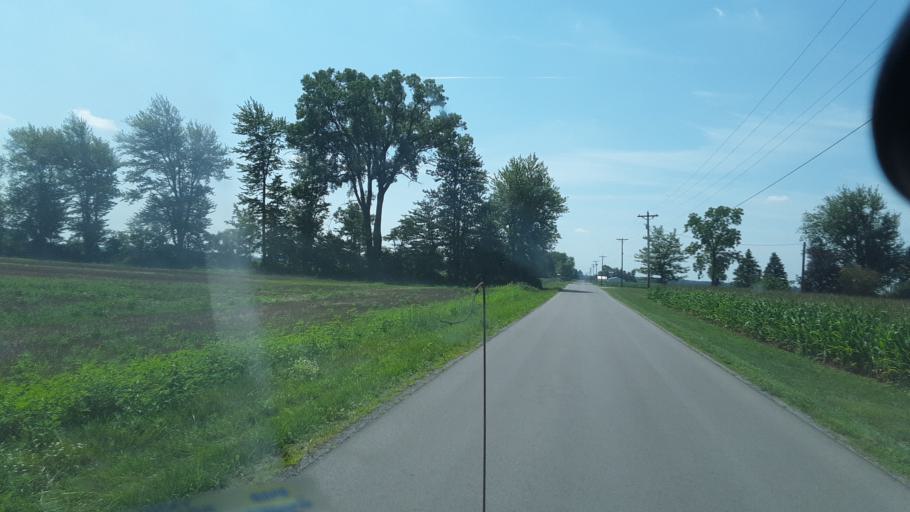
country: US
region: Ohio
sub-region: Hancock County
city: Findlay
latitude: 41.0118
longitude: -83.5159
